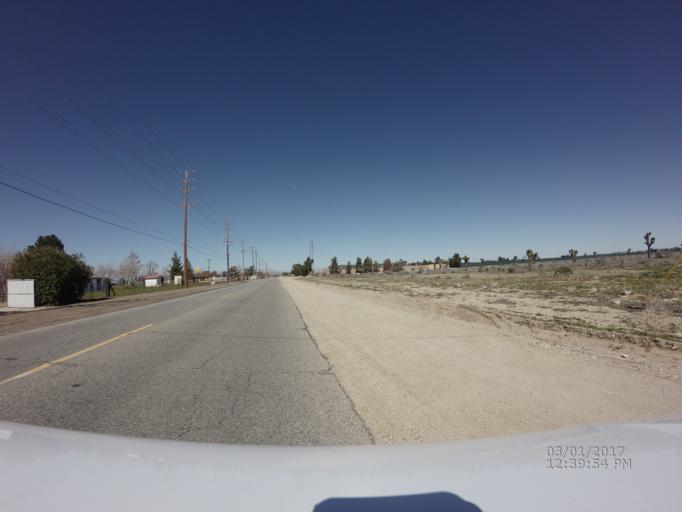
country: US
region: California
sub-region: Los Angeles County
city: Desert View Highlands
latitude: 34.6410
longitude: -118.1657
